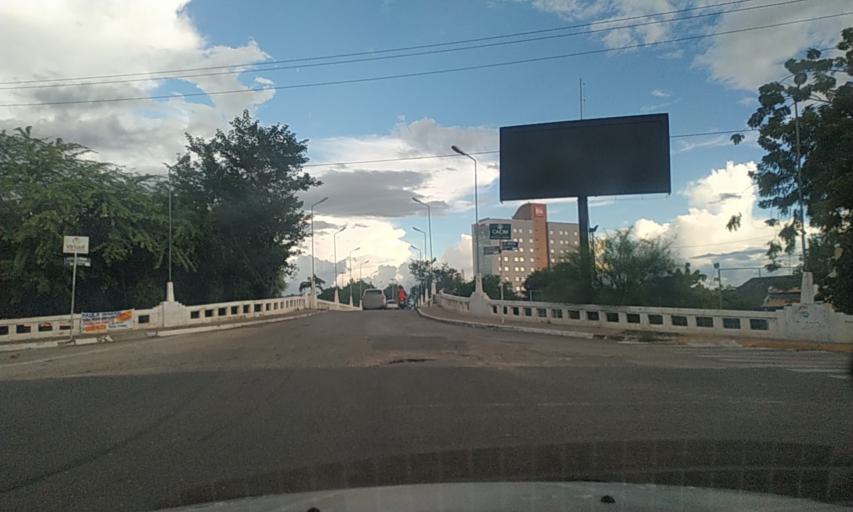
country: BR
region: Rio Grande do Norte
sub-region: Mossoro
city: Mossoro
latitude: -5.1945
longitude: -37.3425
